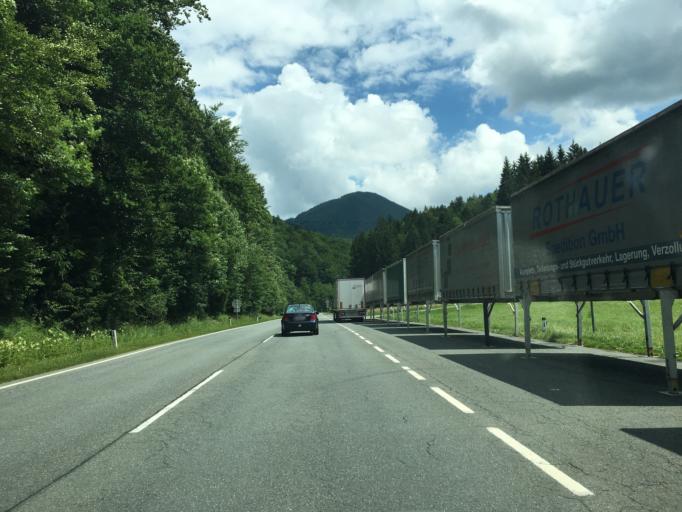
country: AT
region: Salzburg
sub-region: Politischer Bezirk Salzburg-Umgebung
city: Hof bei Salzburg
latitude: 47.8099
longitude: 13.1923
